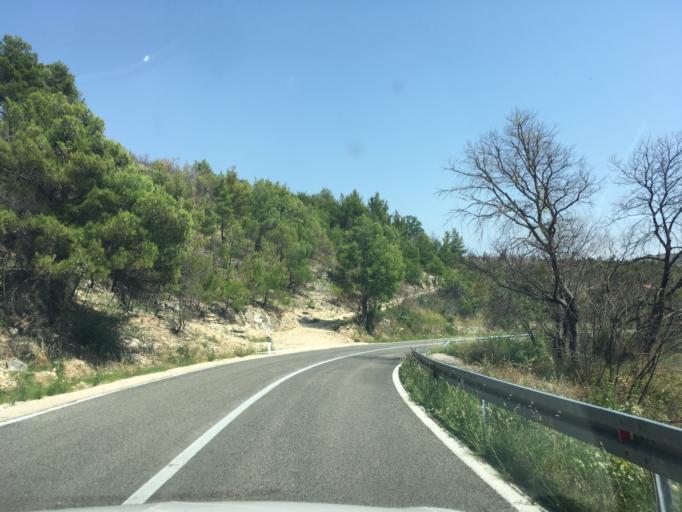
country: HR
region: Sibensko-Kniniska
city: Kistanje
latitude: 43.9392
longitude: 15.8329
